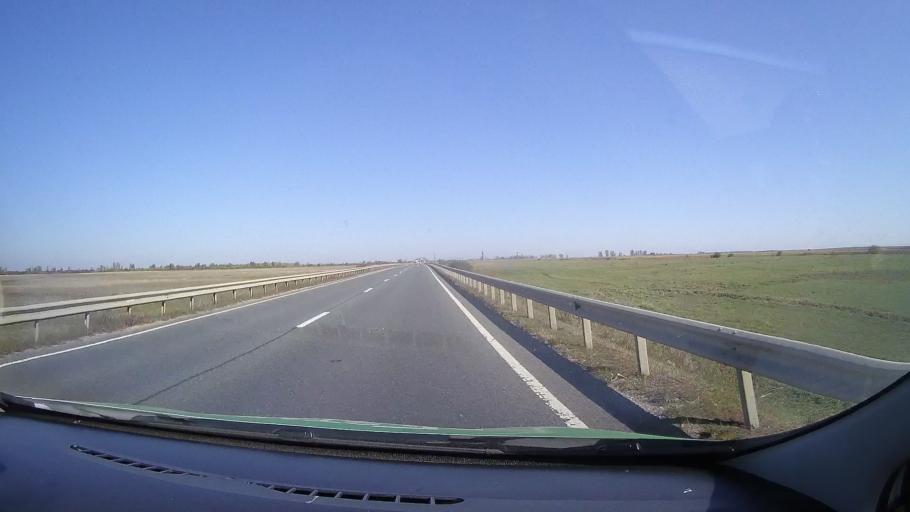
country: RO
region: Satu Mare
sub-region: Comuna Moftinu
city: Moftinu Mic
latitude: 47.6904
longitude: 22.6122
